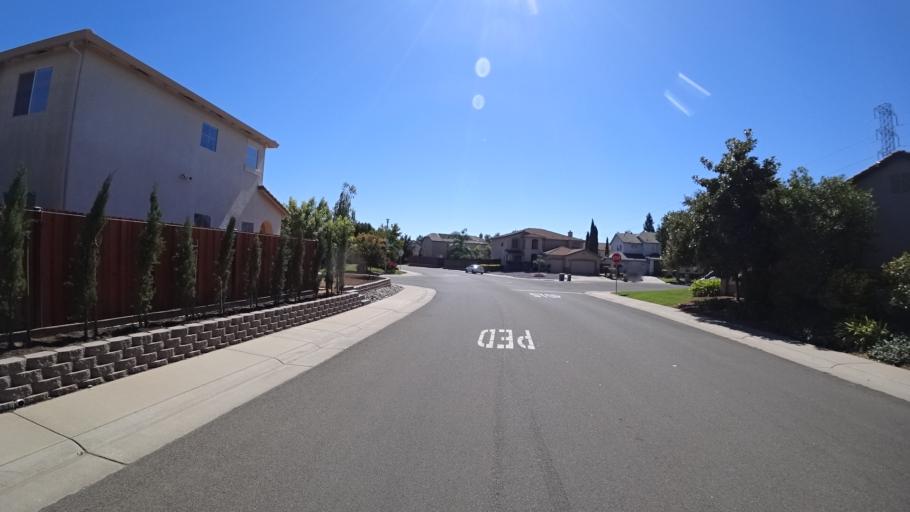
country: US
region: California
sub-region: Sacramento County
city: Elk Grove
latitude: 38.4163
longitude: -121.3492
